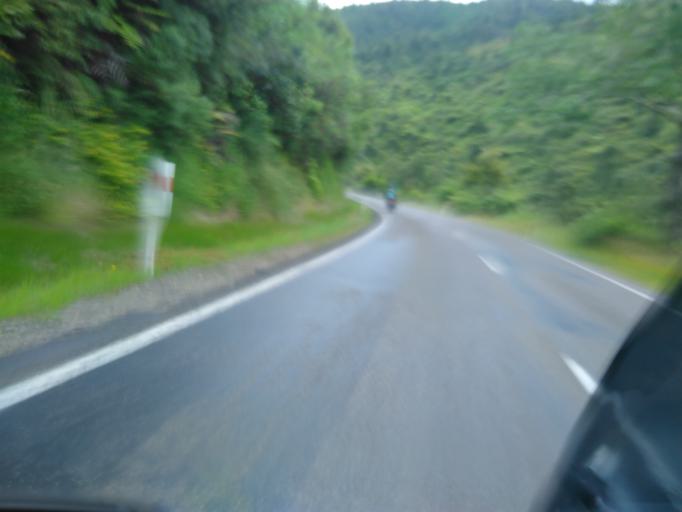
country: NZ
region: Bay of Plenty
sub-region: Opotiki District
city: Opotiki
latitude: -38.2447
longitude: 177.3055
